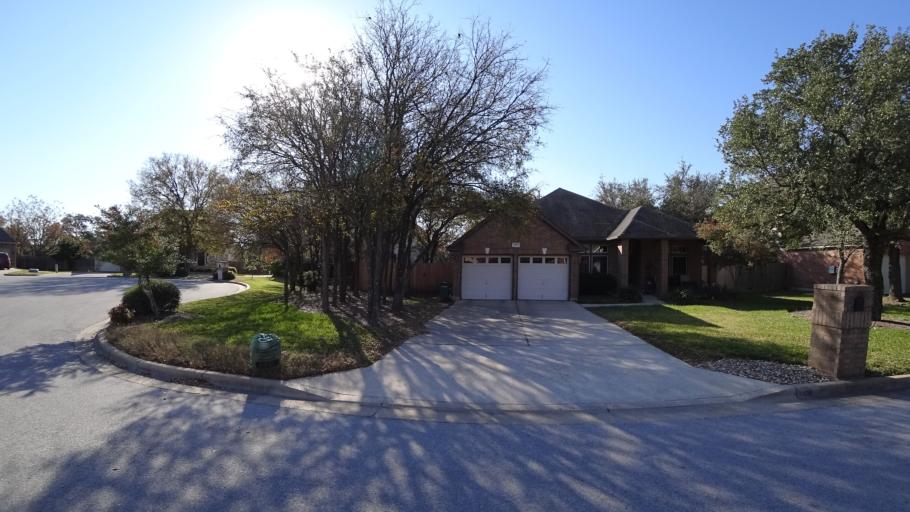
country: US
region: Texas
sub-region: Travis County
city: Shady Hollow
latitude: 30.2244
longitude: -97.8508
